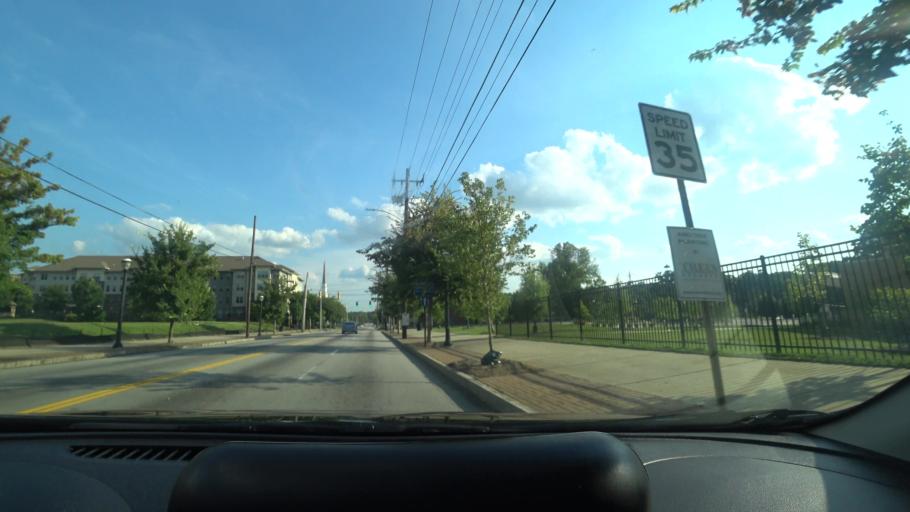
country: US
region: Georgia
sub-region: Fulton County
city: Atlanta
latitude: 33.7149
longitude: -84.3934
